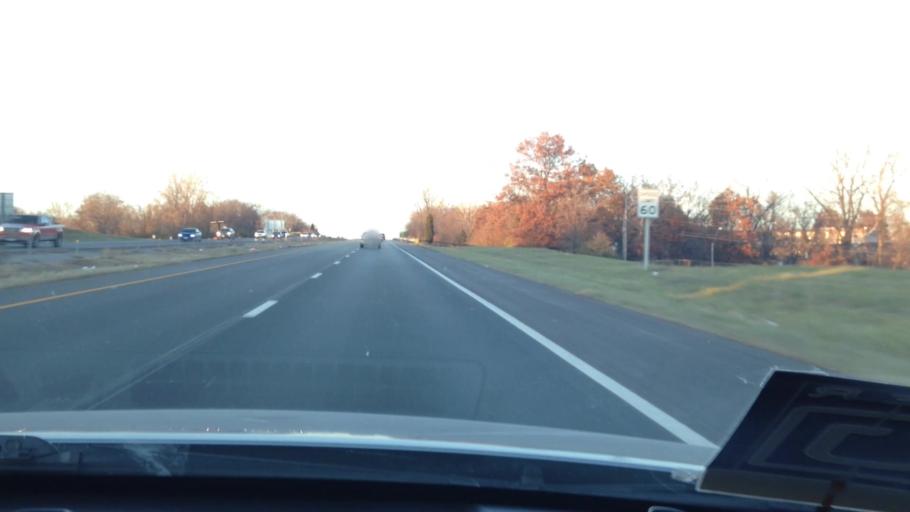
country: US
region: Missouri
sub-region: Platte County
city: Riverside
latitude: 39.2019
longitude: -94.5897
